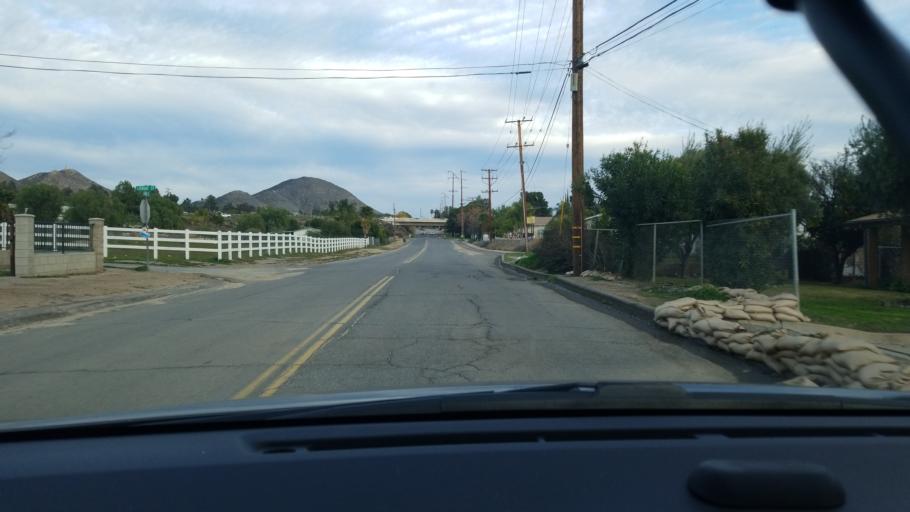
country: US
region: California
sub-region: Riverside County
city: Sedco Hills
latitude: 33.6342
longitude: -117.2821
